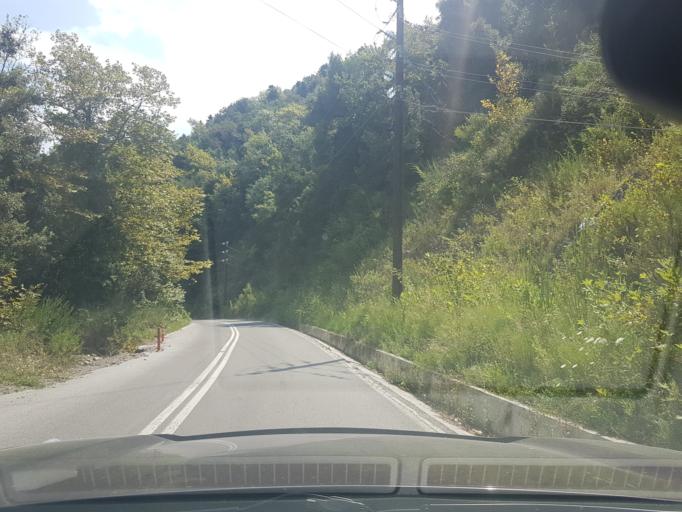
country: GR
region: Central Greece
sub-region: Nomos Evvoias
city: Kymi
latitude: 38.6387
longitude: 23.9397
